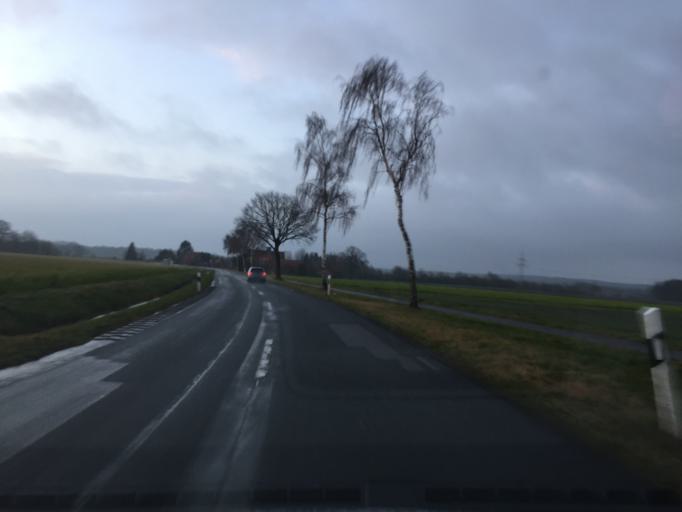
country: DE
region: Lower Saxony
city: Pennigsehl
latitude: 52.6344
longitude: 9.0227
